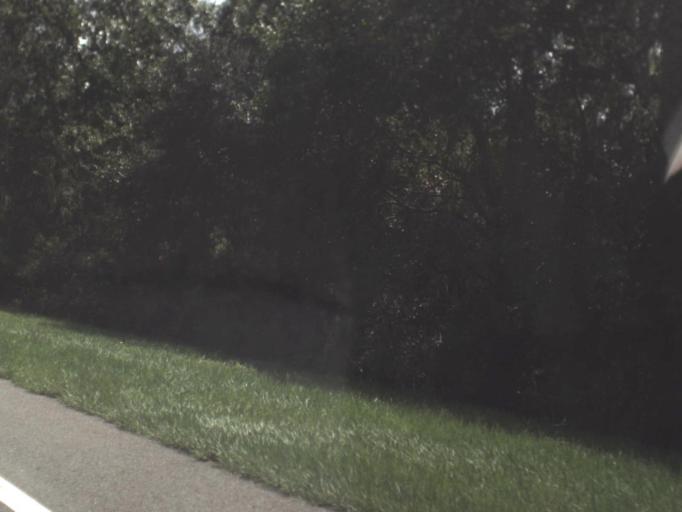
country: US
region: Florida
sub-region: Sarasota County
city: The Meadows
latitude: 27.4142
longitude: -82.3485
